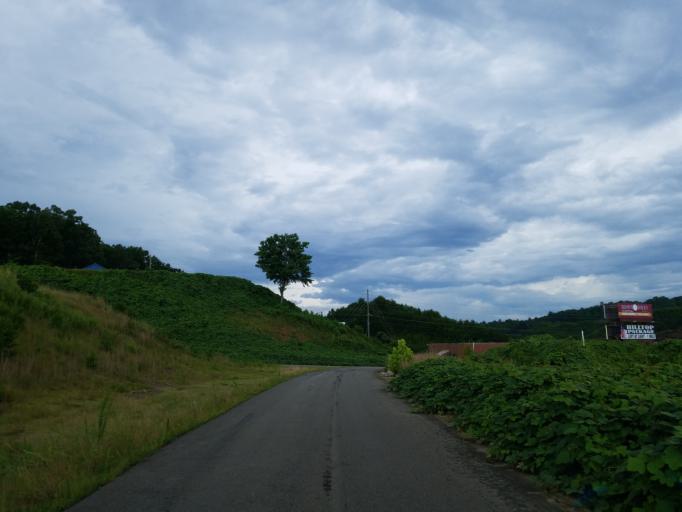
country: US
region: Georgia
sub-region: Gilmer County
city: Ellijay
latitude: 34.6640
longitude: -84.4900
